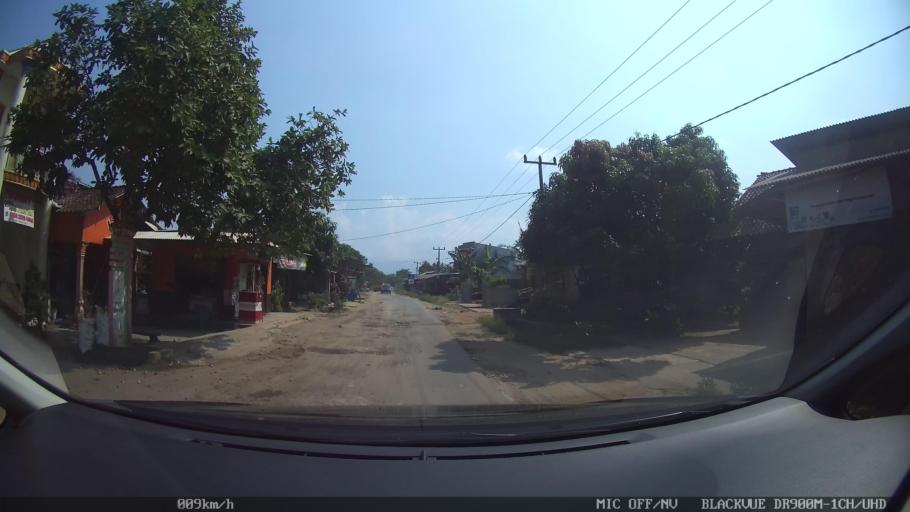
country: ID
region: Lampung
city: Natar
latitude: -5.2974
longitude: 105.2257
